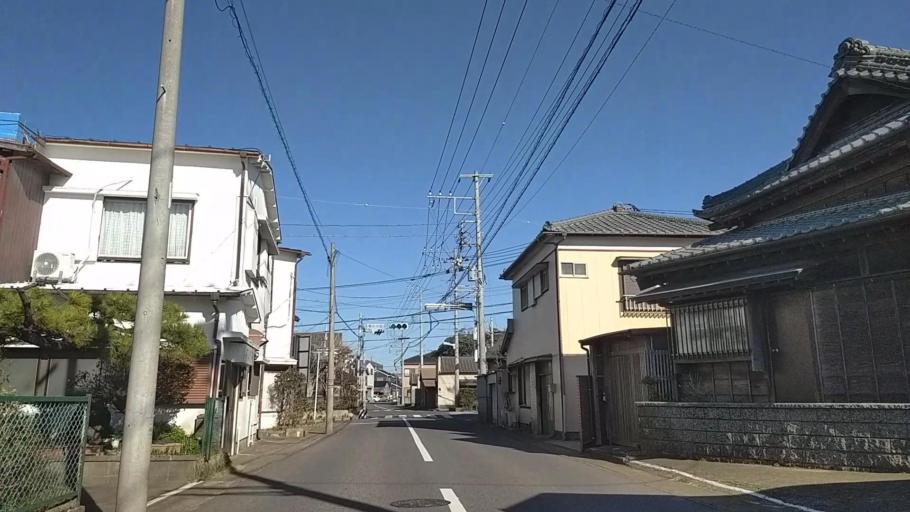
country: JP
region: Chiba
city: Hasaki
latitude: 35.7235
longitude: 140.8344
